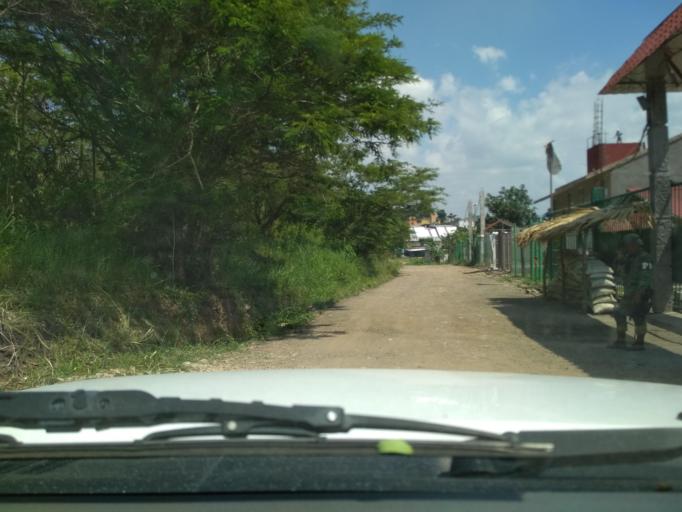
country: MX
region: Veracruz
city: Cordoba
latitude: 18.8752
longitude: -96.9118
